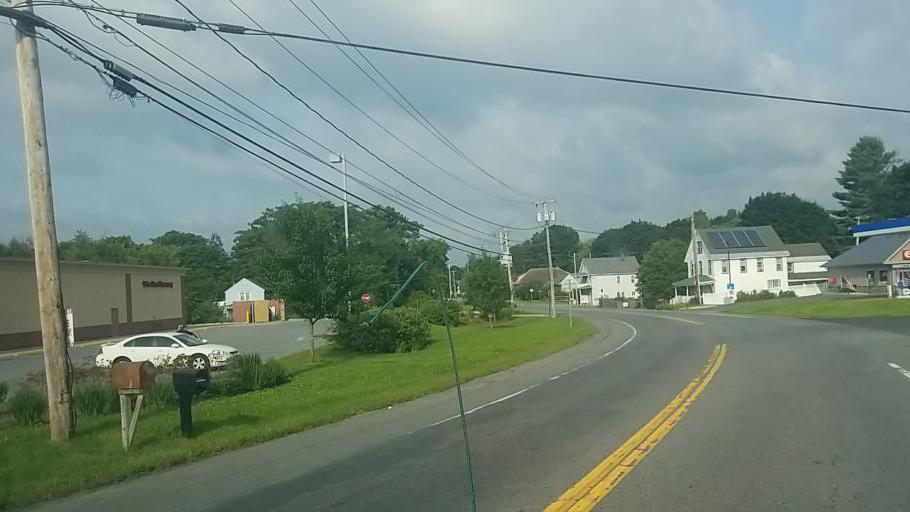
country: US
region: New York
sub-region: Fulton County
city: Gloversville
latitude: 43.0514
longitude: -74.3227
